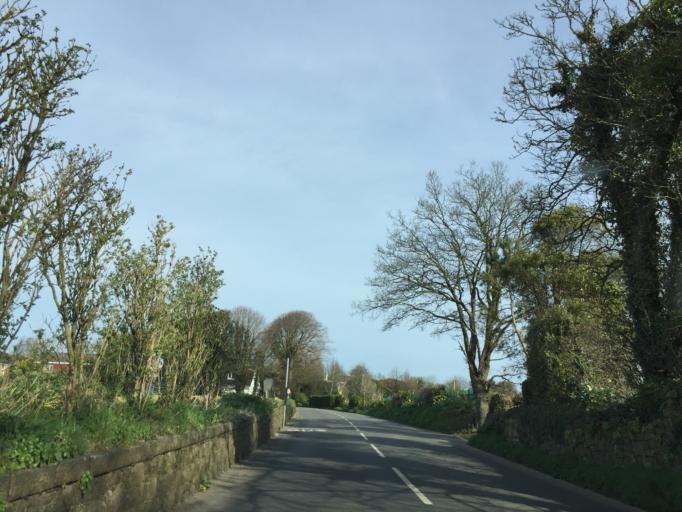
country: JE
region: St Helier
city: Saint Helier
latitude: 49.2215
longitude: -2.1415
